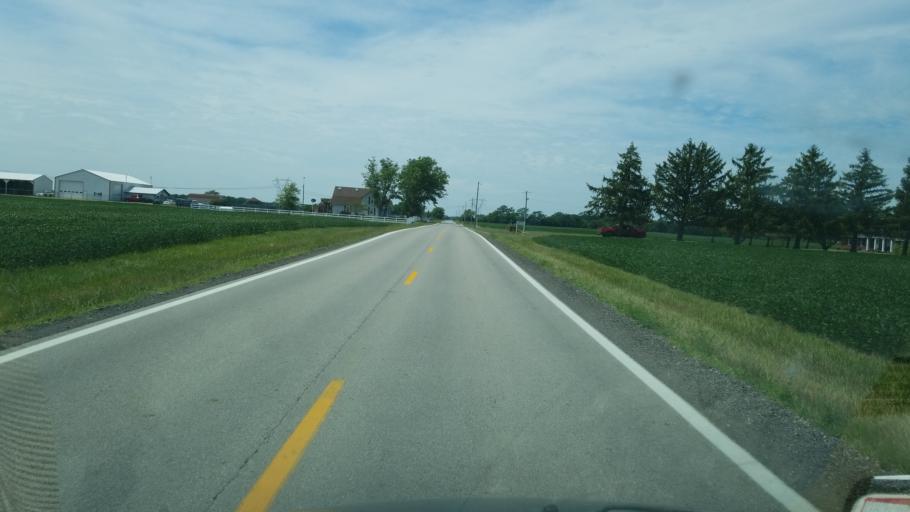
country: US
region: Ohio
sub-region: Madison County
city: West Jefferson
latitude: 39.8717
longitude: -83.2934
